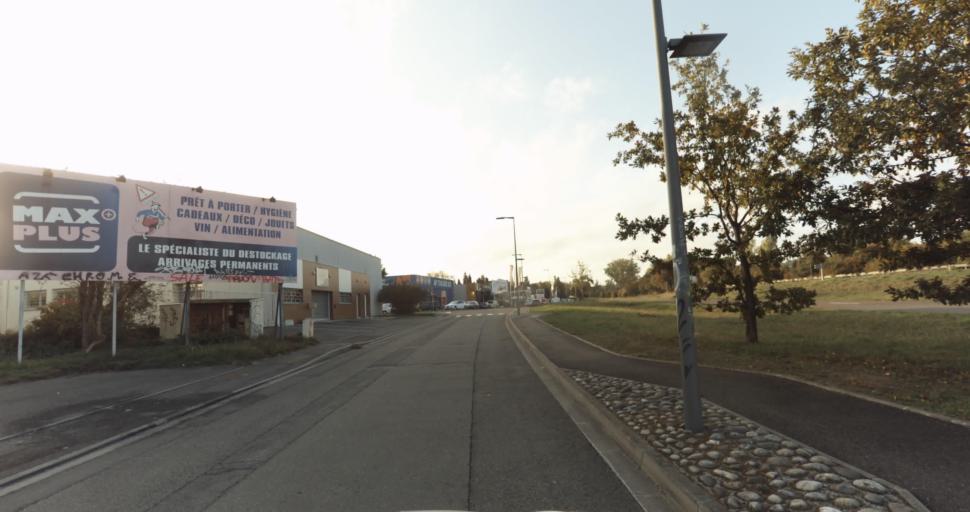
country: FR
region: Midi-Pyrenees
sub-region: Departement de la Haute-Garonne
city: Ramonville-Saint-Agne
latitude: 43.5534
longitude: 1.4783
